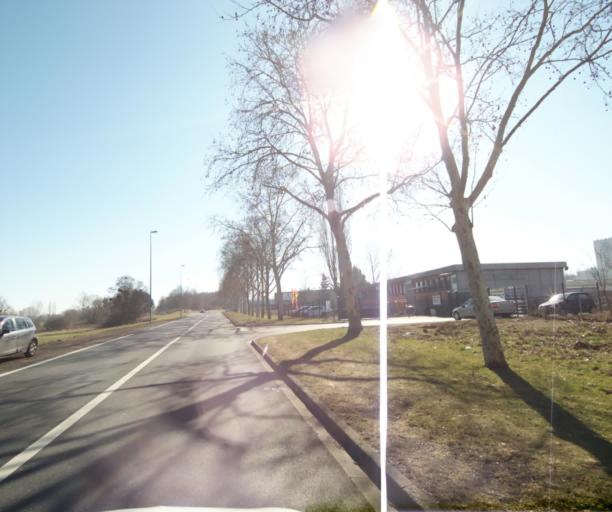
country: FR
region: Lorraine
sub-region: Departement de Meurthe-et-Moselle
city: Jarville-la-Malgrange
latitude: 48.6708
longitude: 6.2123
